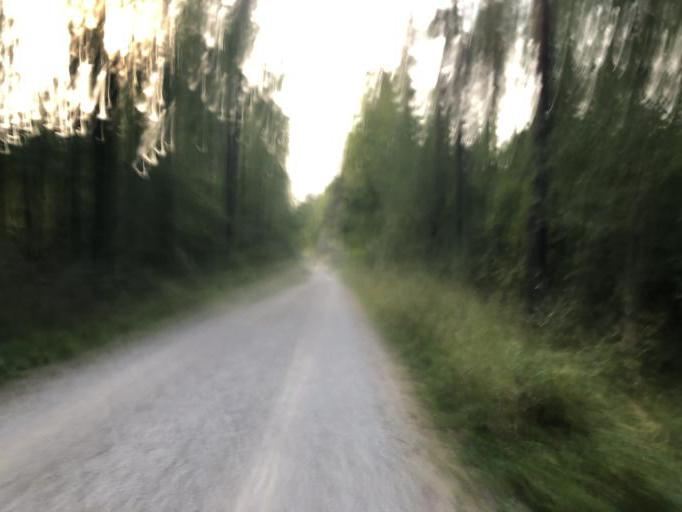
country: DE
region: Bavaria
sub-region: Regierungsbezirk Mittelfranken
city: Buckenhof
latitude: 49.5776
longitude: 11.0418
